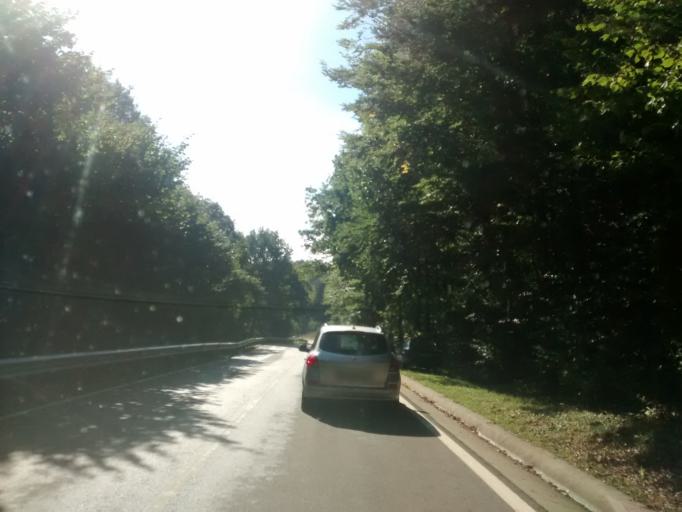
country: ES
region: Cantabria
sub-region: Provincia de Cantabria
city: Reinosa
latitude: 42.9475
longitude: -4.0531
